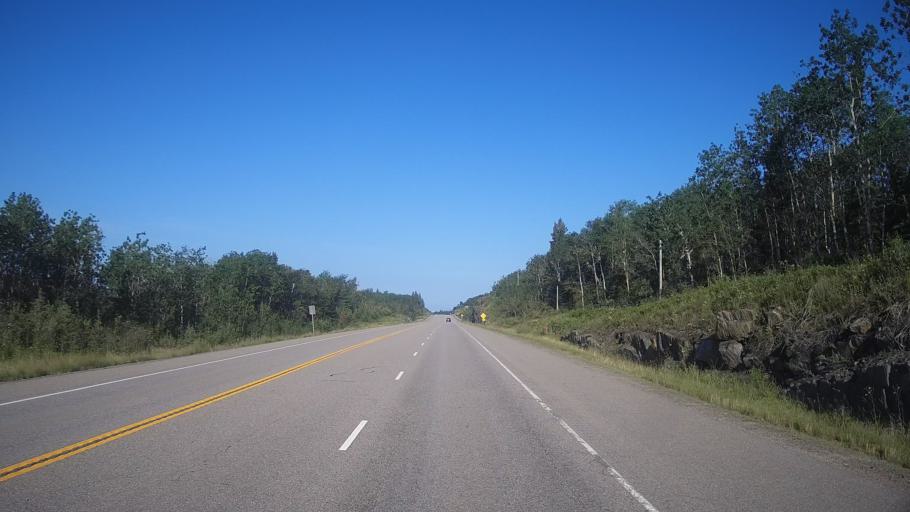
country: US
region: Minnesota
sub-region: Roseau County
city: Warroad
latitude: 49.7179
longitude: -94.7388
